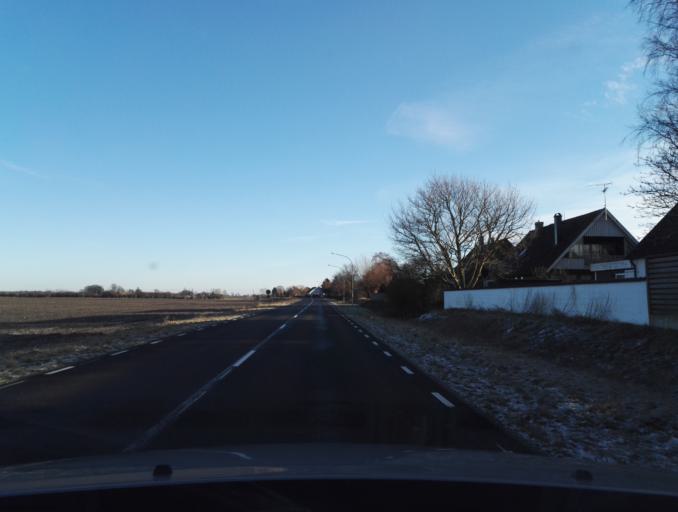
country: SE
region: Skane
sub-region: Trelleborgs Kommun
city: Skare
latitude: 55.3781
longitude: 13.0483
